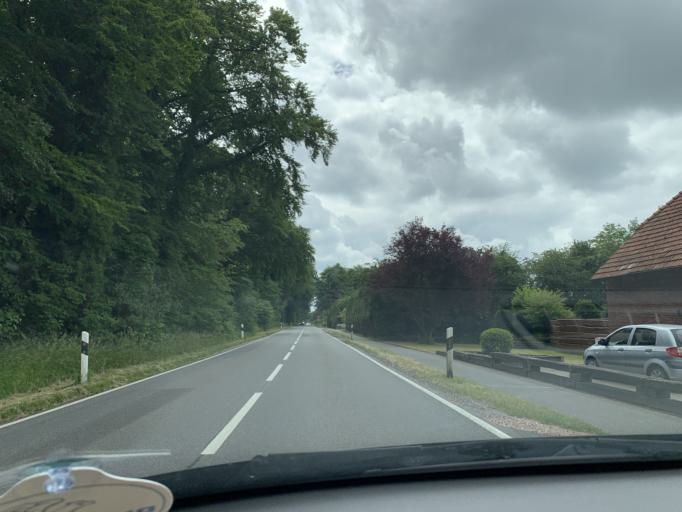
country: DE
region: Lower Saxony
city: Bockhorn
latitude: 53.3706
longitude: 8.0585
